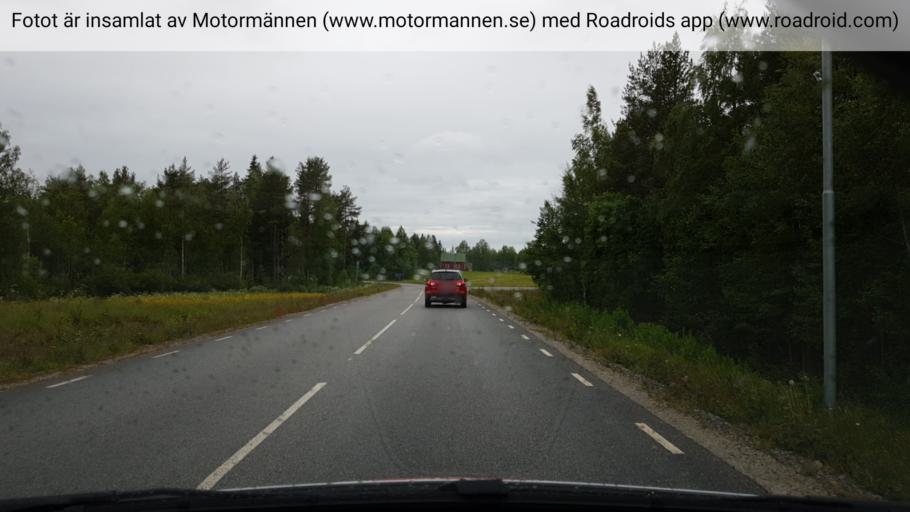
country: SE
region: Vaesterbotten
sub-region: Bjurholms Kommun
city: Bjurholm
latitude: 64.1459
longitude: 19.3181
